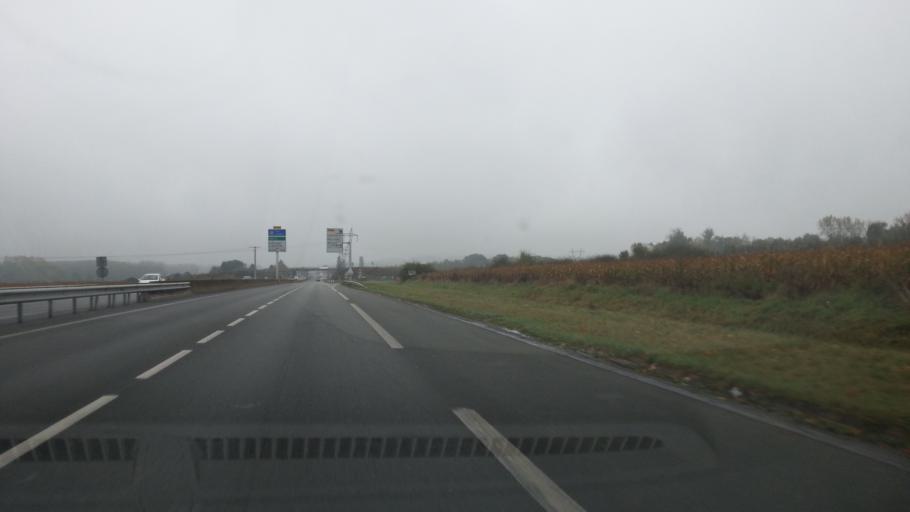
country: FR
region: Picardie
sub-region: Departement de l'Oise
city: Breuil-le-Vert
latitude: 49.3540
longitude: 2.4263
